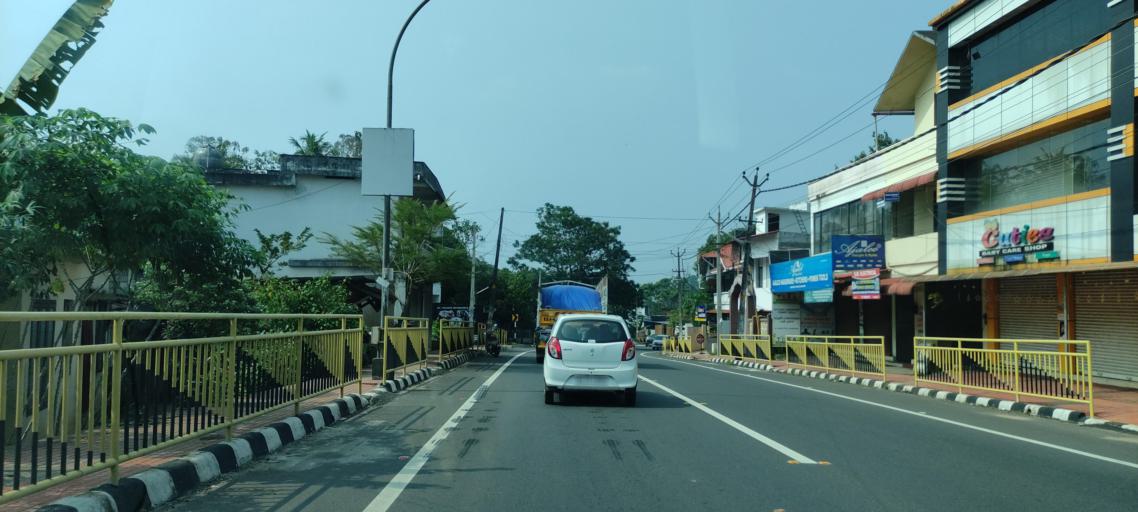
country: IN
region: Kerala
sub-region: Alappuzha
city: Chengannur
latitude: 9.2457
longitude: 76.6698
